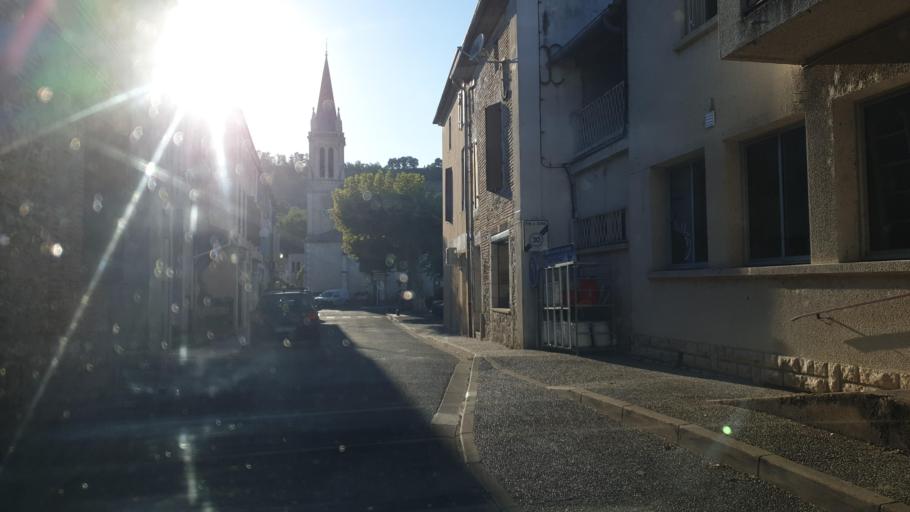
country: FR
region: Aquitaine
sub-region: Departement du Lot-et-Garonne
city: Castelmoron-sur-Lot
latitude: 44.3969
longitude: 0.4957
